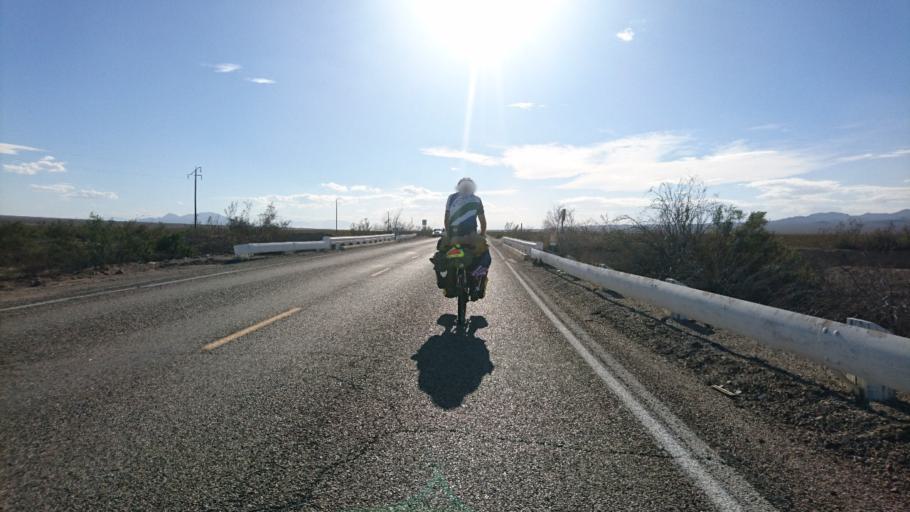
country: US
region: California
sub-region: San Bernardino County
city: Needles
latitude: 34.7118
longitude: -115.2820
